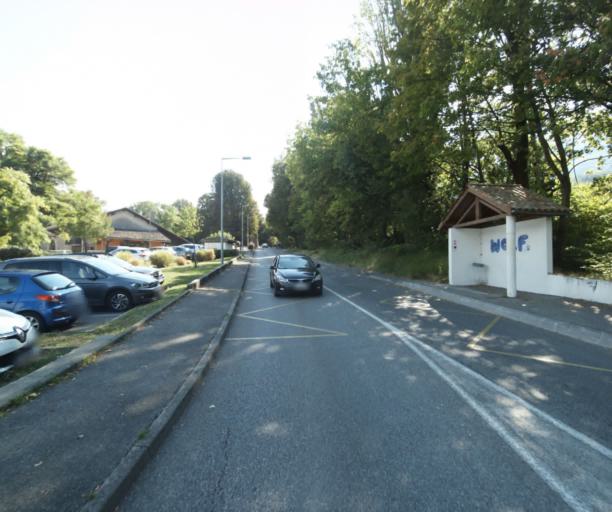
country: FR
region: Rhone-Alpes
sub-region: Departement de l'Isere
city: Seyssinet-Pariset
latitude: 45.1655
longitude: 5.6887
